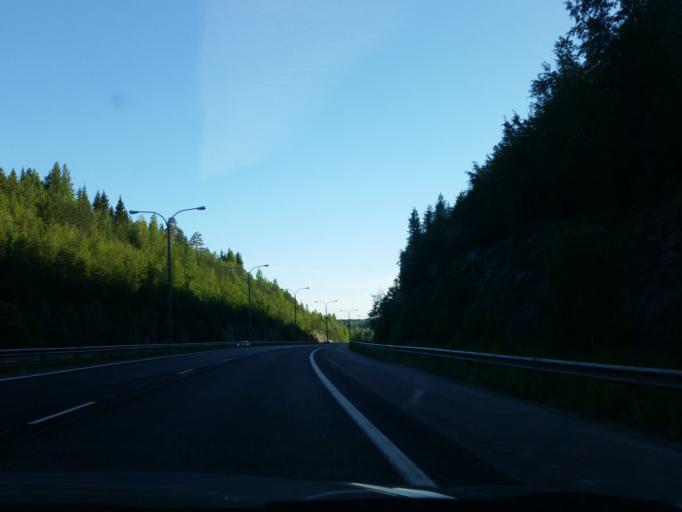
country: FI
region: Northern Savo
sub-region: Kuopio
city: Kuopio
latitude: 62.8468
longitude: 27.6175
